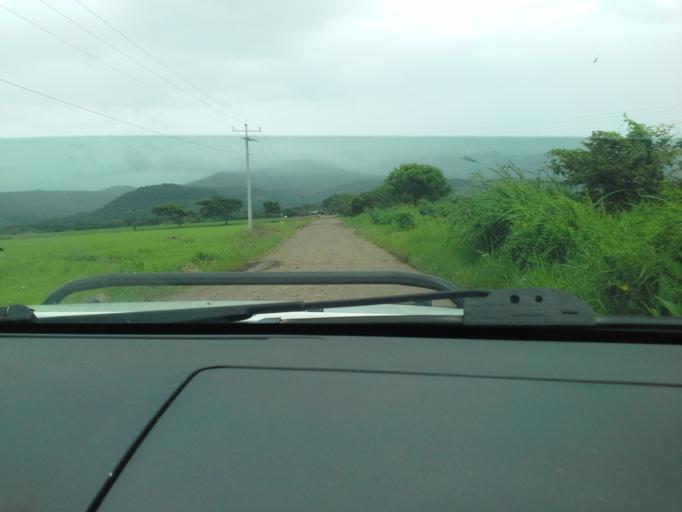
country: NI
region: Matagalpa
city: Ciudad Dario
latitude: 12.8592
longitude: -86.1843
